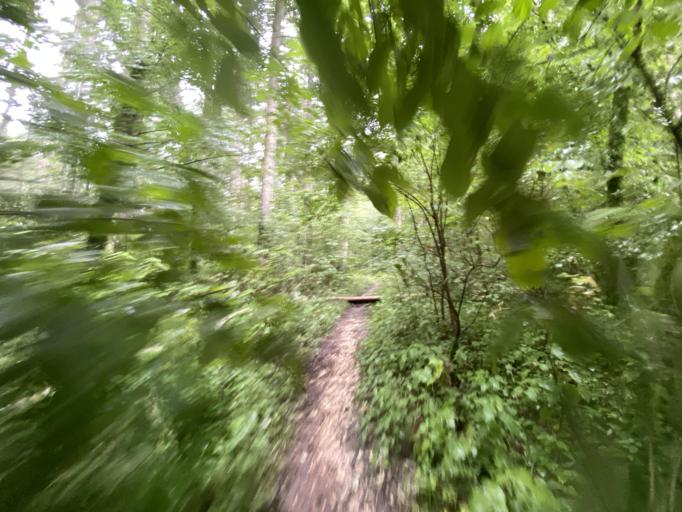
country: DE
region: Baden-Wuerttemberg
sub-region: Tuebingen Region
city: Bingen
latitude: 48.1146
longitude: 9.2624
